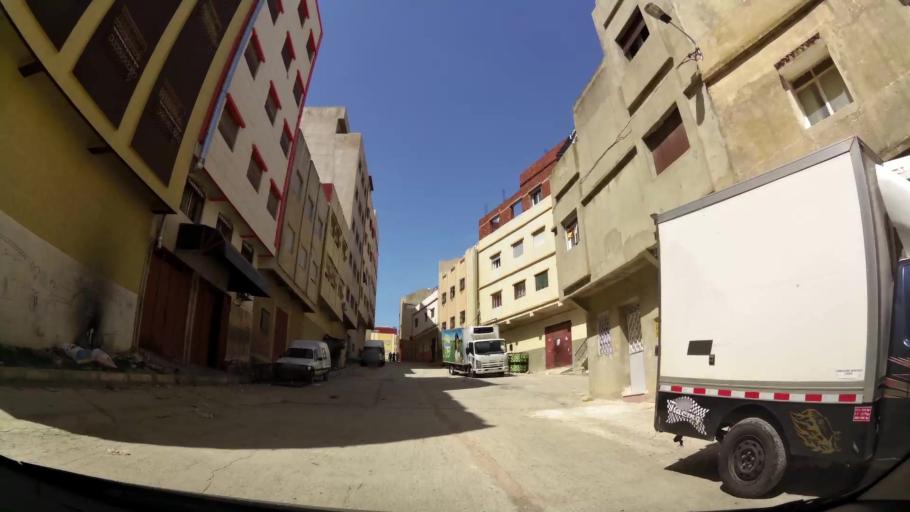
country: MA
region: Tanger-Tetouan
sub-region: Tanger-Assilah
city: Tangier
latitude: 35.7341
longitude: -5.8075
